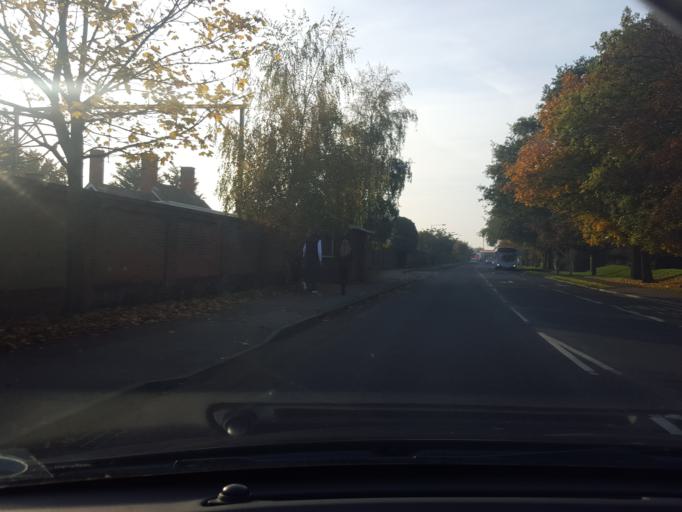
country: GB
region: England
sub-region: Essex
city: Frinton-on-Sea
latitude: 51.8378
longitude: 1.2441
